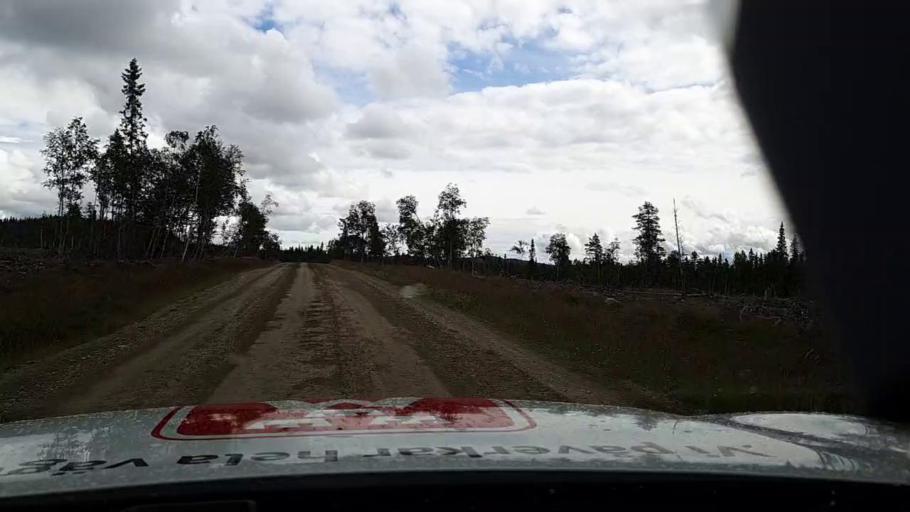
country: SE
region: Jaemtland
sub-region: Are Kommun
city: Jarpen
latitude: 62.6103
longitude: 13.2048
